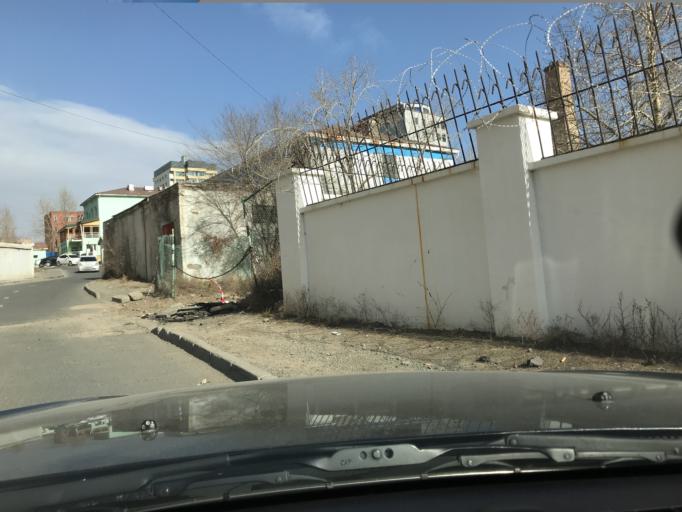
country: MN
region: Ulaanbaatar
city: Ulaanbaatar
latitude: 47.9195
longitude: 106.9400
